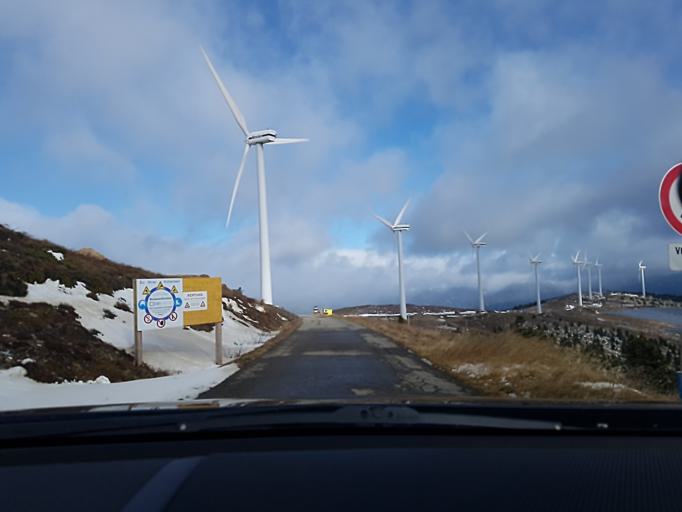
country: AT
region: Styria
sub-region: Politischer Bezirk Murtal
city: Pusterwald
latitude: 47.2695
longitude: 14.3821
